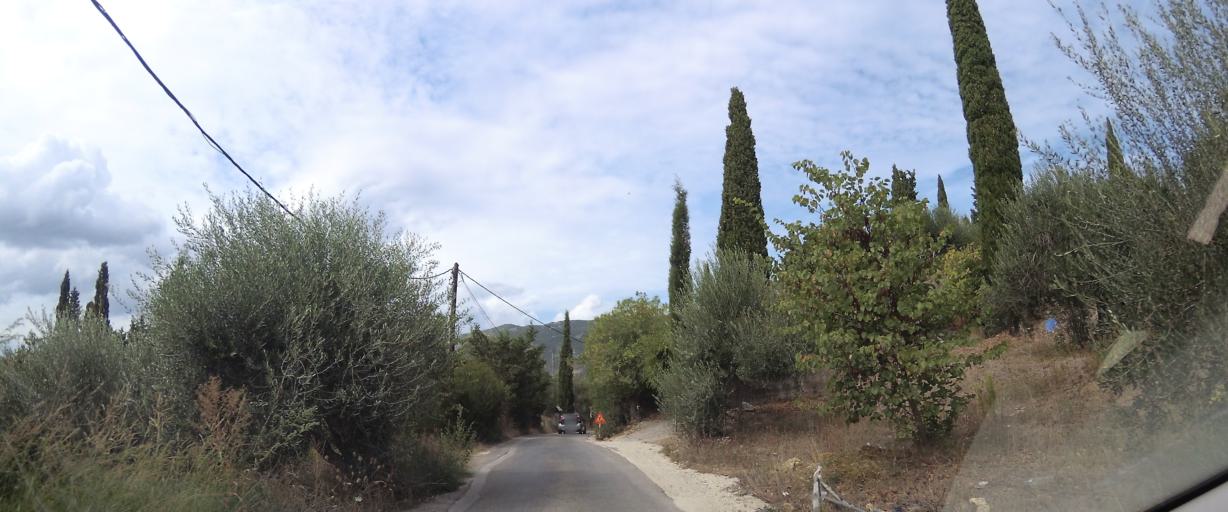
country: GR
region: Ionian Islands
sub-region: Nomos Kerkyras
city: Kontokali
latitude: 39.6939
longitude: 19.8091
